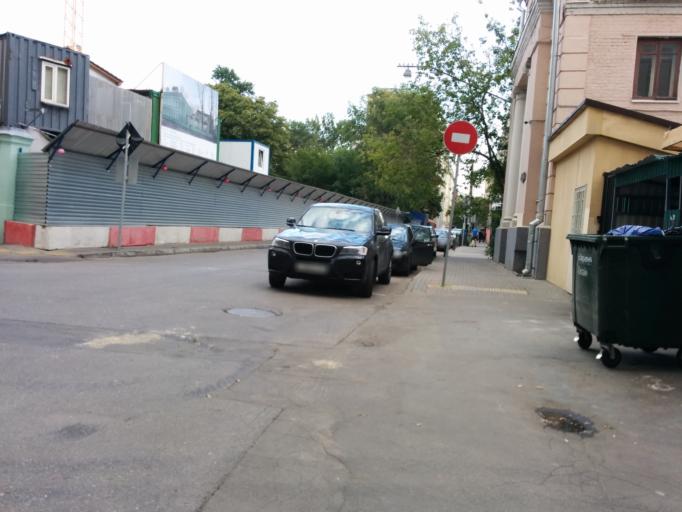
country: RU
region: Moscow
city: Moscow
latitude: 55.7651
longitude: 37.6399
